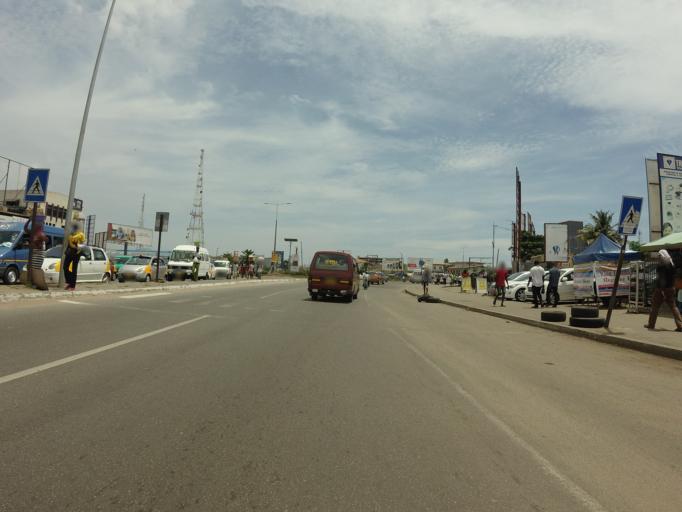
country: GH
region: Greater Accra
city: Accra
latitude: 5.5618
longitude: -0.2302
